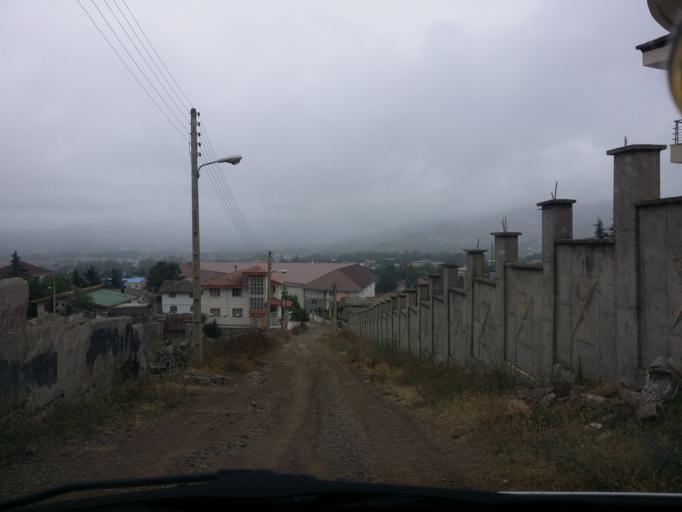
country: IR
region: Mazandaran
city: `Abbasabad
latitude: 36.5094
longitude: 51.1544
